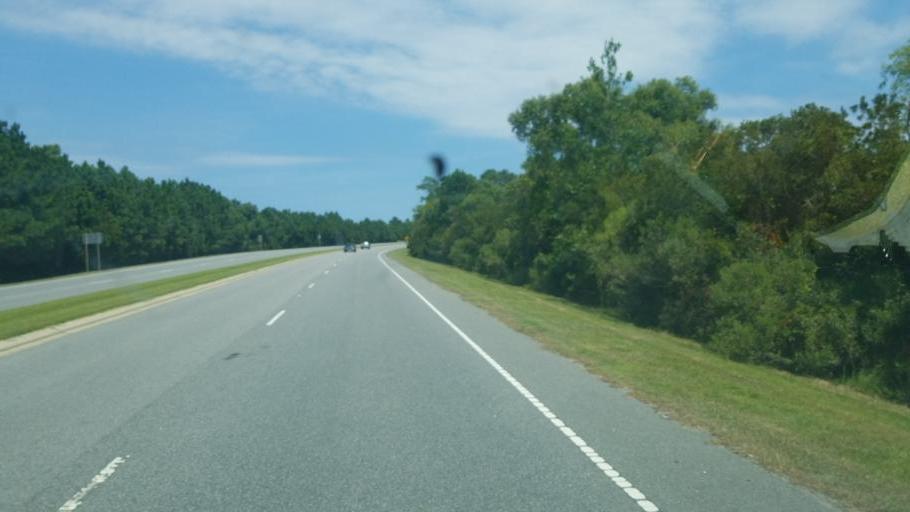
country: US
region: North Carolina
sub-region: Dare County
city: Manteo
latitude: 35.8880
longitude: -75.6656
